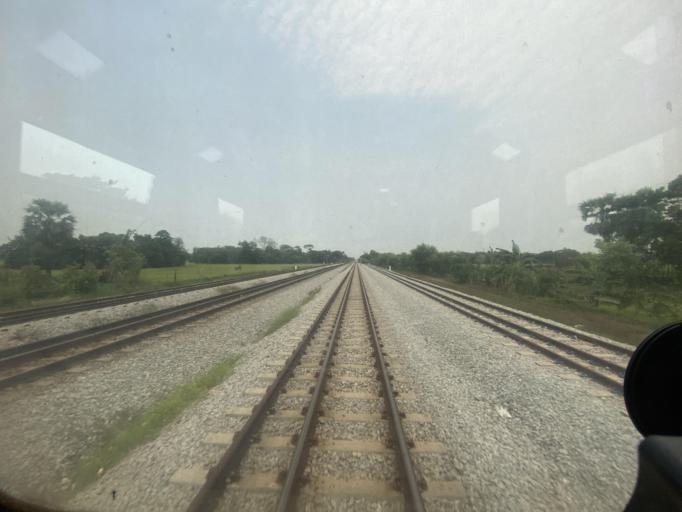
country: BD
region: Chittagong
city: Laksham
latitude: 23.3084
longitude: 91.1390
